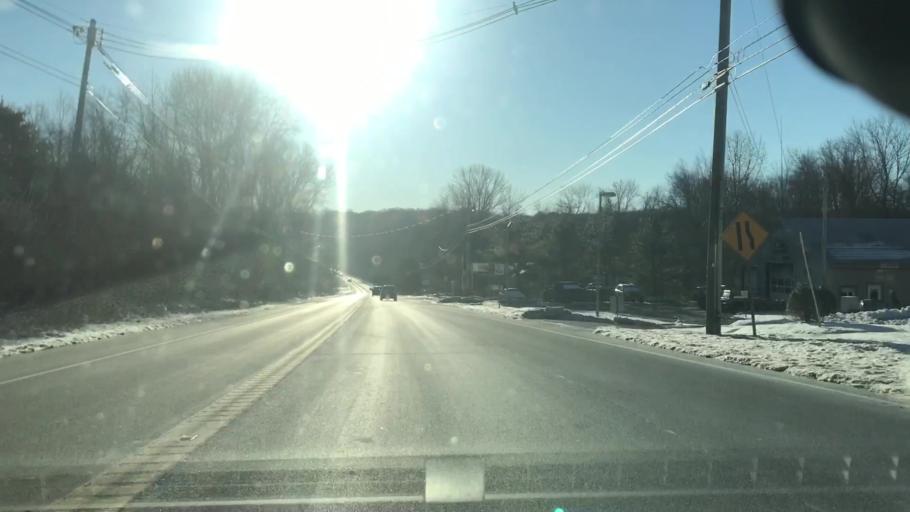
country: US
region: New Jersey
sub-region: Morris County
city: Chester
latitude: 40.8016
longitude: -74.7130
